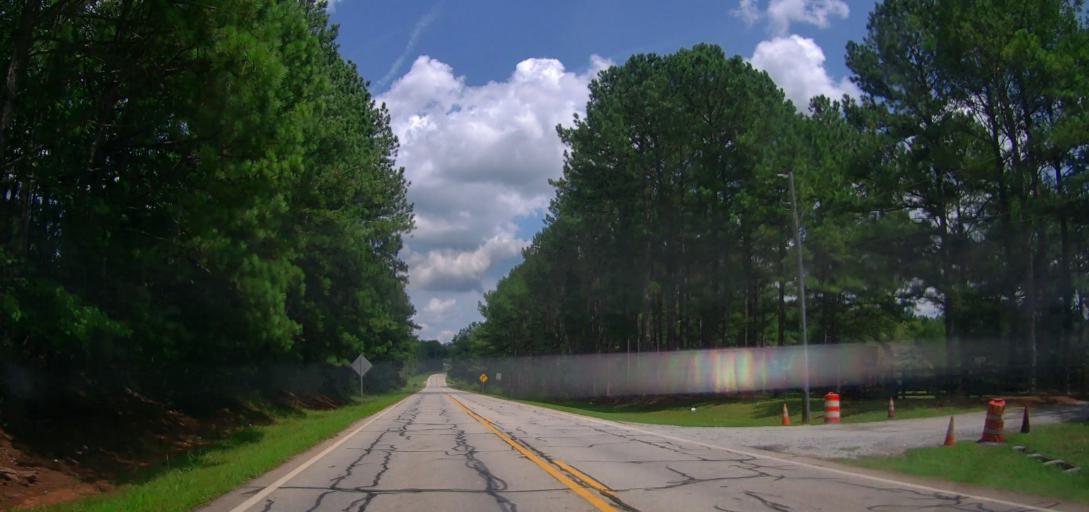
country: US
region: Georgia
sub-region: Troup County
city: Hogansville
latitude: 33.2327
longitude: -84.9551
